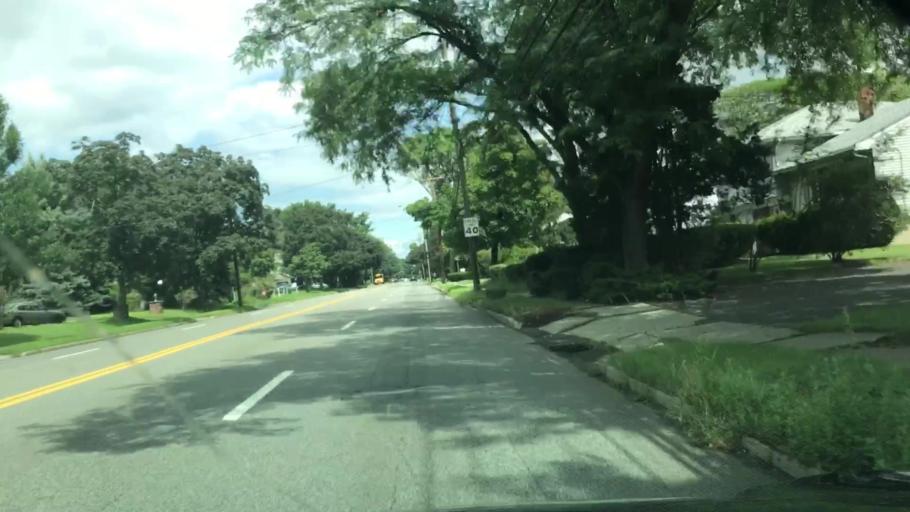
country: US
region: New Jersey
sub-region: Bergen County
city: River Edge
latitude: 40.9399
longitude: -74.0512
